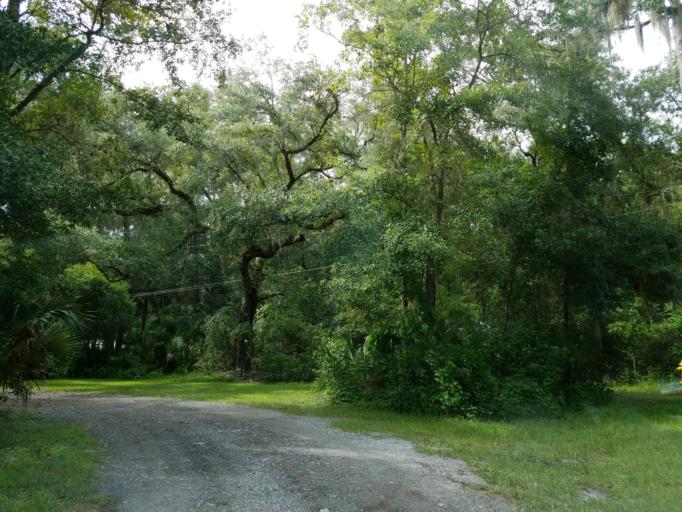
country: US
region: Florida
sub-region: Alachua County
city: Gainesville
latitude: 29.5040
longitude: -82.2732
